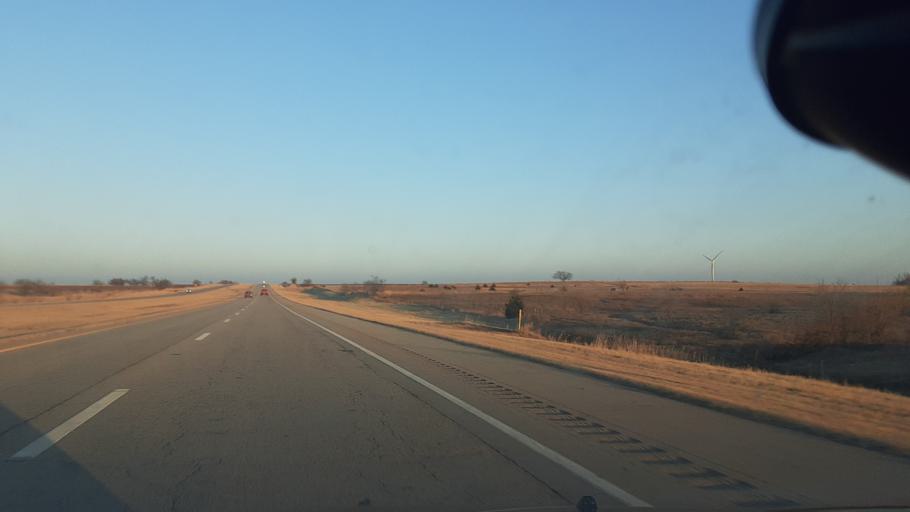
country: US
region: Oklahoma
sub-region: Noble County
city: Perry
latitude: 36.3980
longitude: -97.3862
